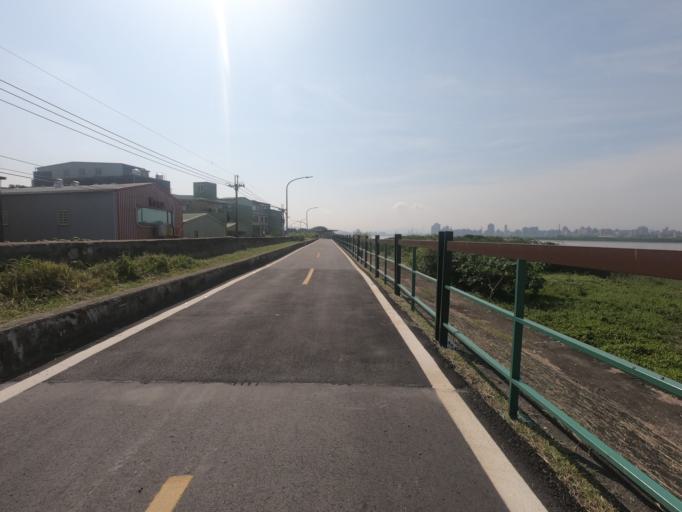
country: TW
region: Taipei
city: Taipei
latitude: 25.1065
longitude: 121.4718
